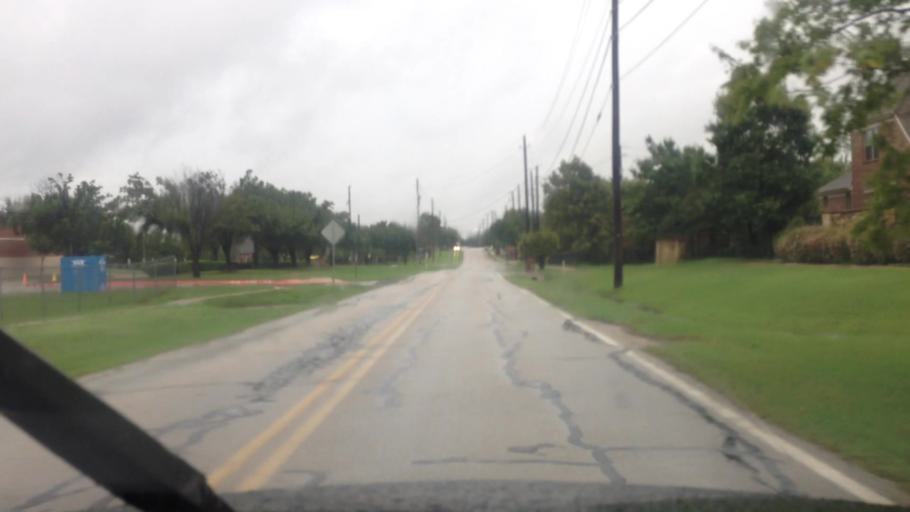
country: US
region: Texas
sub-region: Tarrant County
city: Keller
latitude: 32.9076
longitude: -97.2186
